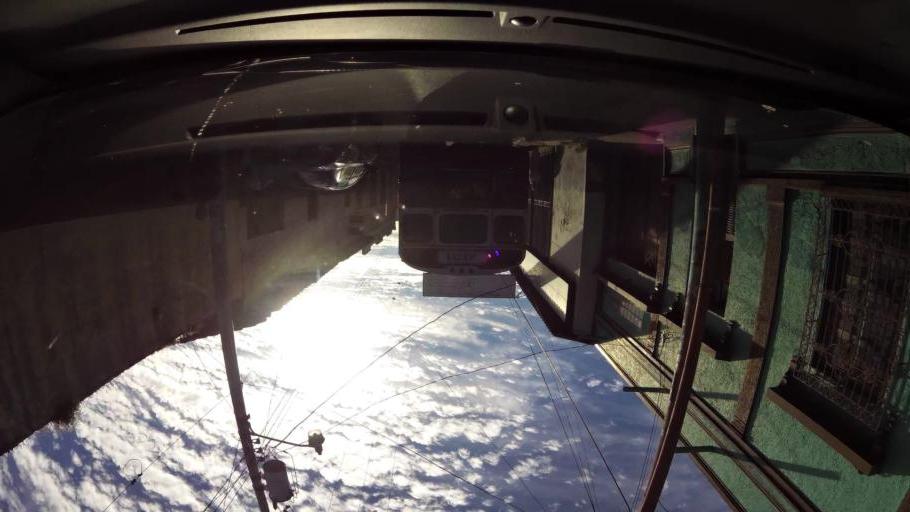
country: SV
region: Santa Ana
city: Santa Ana
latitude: 13.9968
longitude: -89.5578
